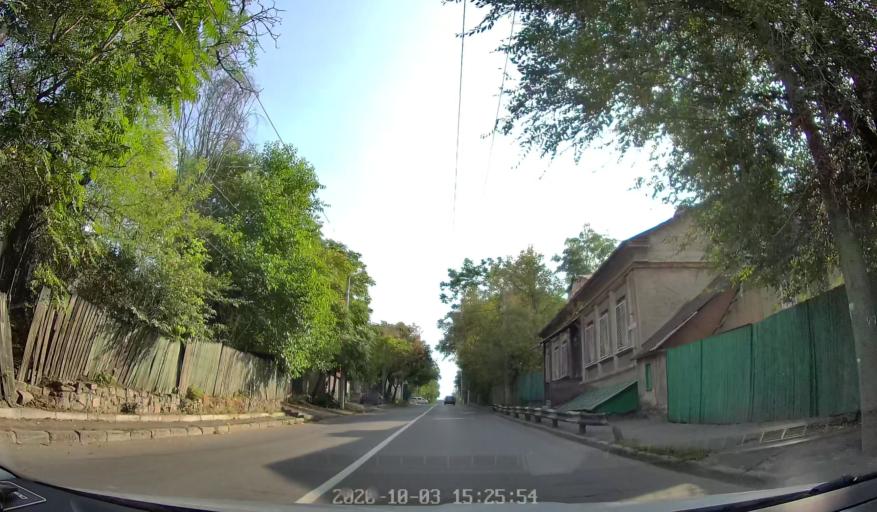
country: MD
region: Chisinau
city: Chisinau
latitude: 47.0322
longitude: 28.8166
